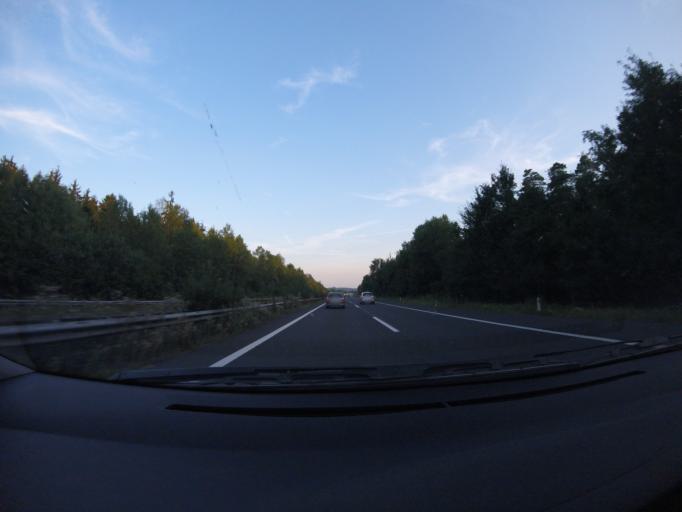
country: AT
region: Styria
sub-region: Politischer Bezirk Hartberg-Fuerstenfeld
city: Hainersdorf
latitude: 47.1082
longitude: 15.9849
